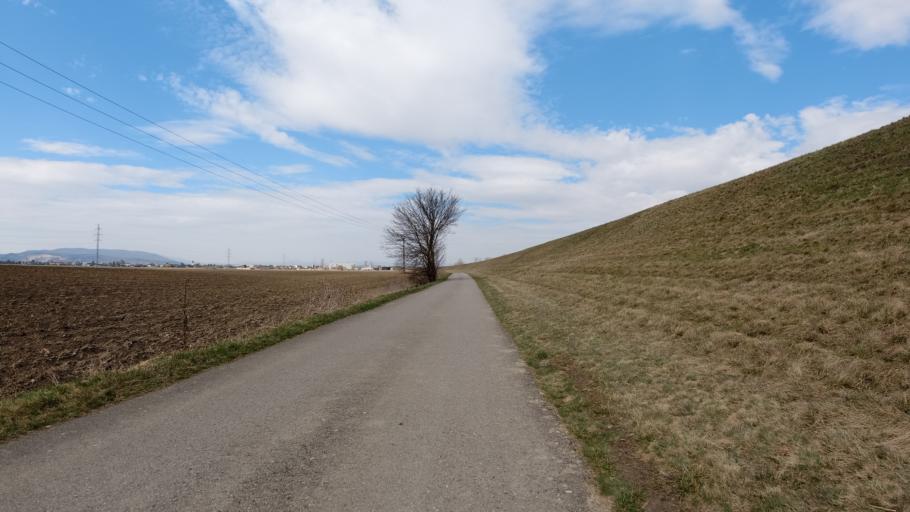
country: SK
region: Nitriansky
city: Cachtice
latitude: 48.6782
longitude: 17.8621
